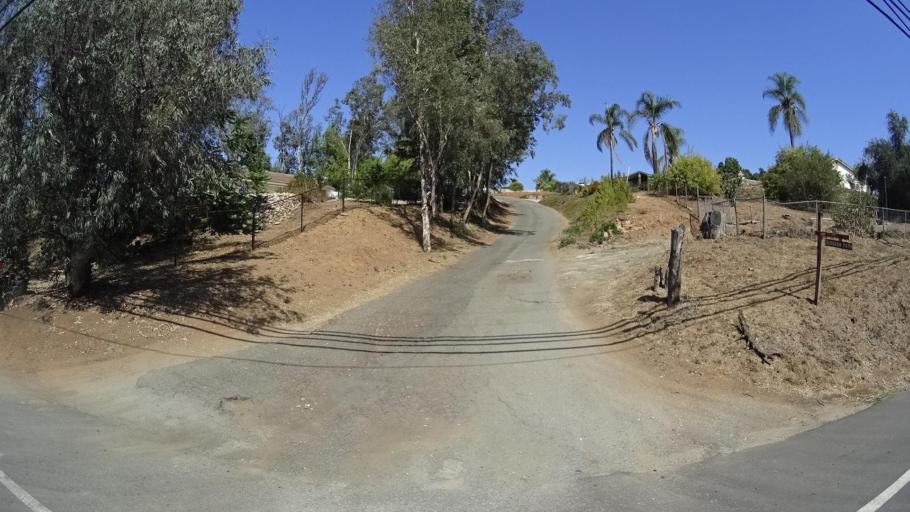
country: US
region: California
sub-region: San Diego County
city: Granite Hills
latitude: 32.7869
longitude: -116.9148
